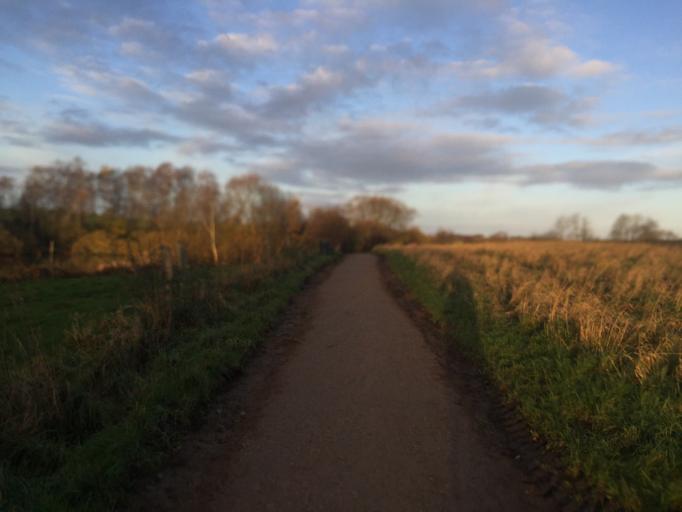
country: DK
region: Zealand
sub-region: Ringsted Kommune
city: Ringsted
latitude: 55.4213
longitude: 11.7778
